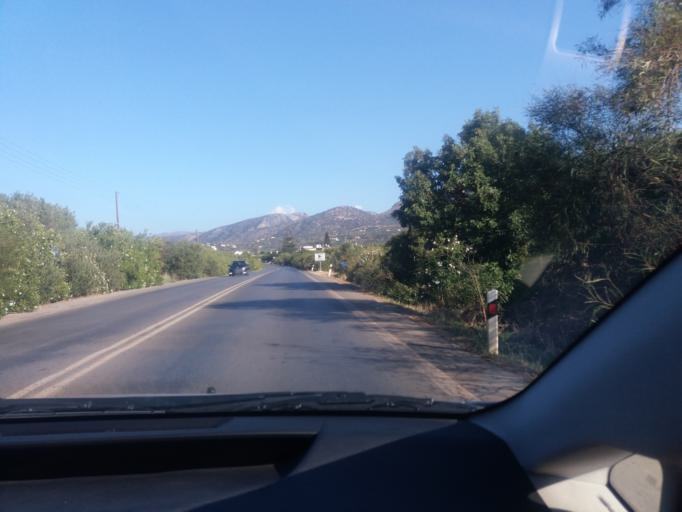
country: GR
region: Crete
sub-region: Nomos Irakleiou
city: Malia
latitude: 35.2897
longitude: 25.4928
